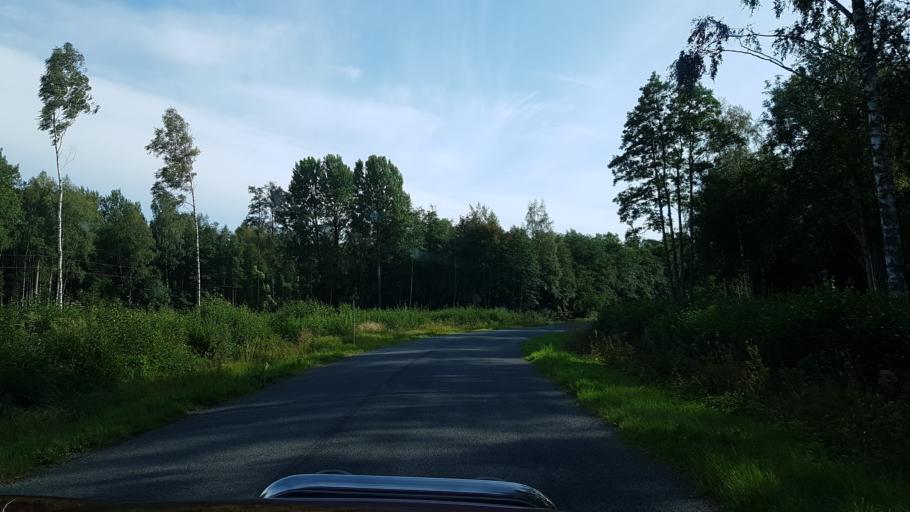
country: EE
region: Laeaene
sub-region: Lihula vald
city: Lihula
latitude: 58.4097
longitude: 24.0157
